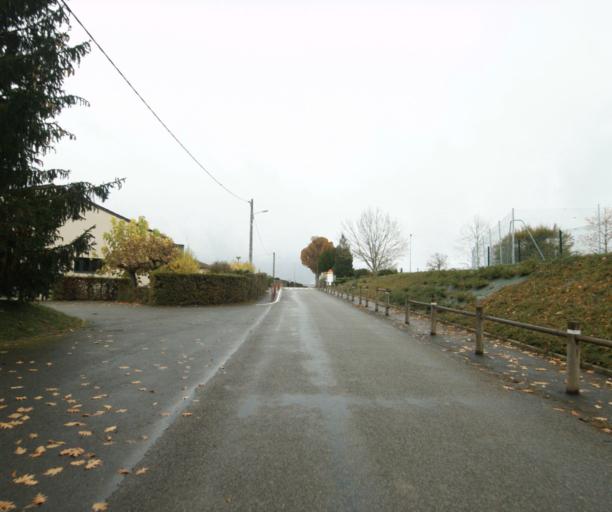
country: FR
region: Rhone-Alpes
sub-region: Departement de l'Ain
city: Pont-de-Vaux
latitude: 46.4773
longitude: 4.8751
